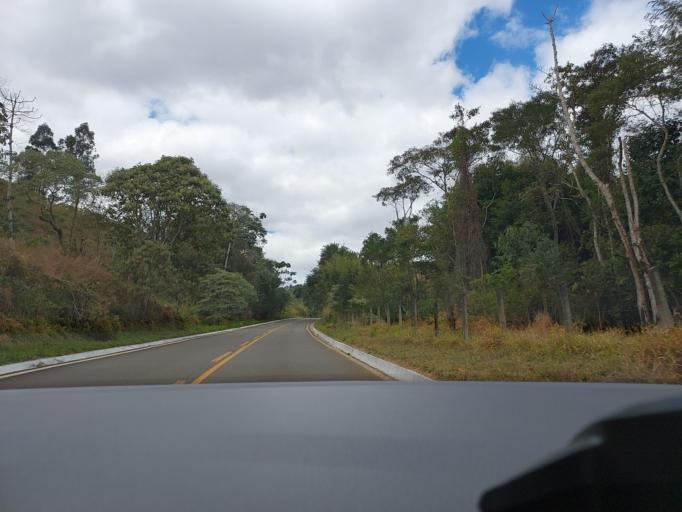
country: BR
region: Minas Gerais
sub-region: Mirai
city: Mirai
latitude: -20.9552
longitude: -42.6014
